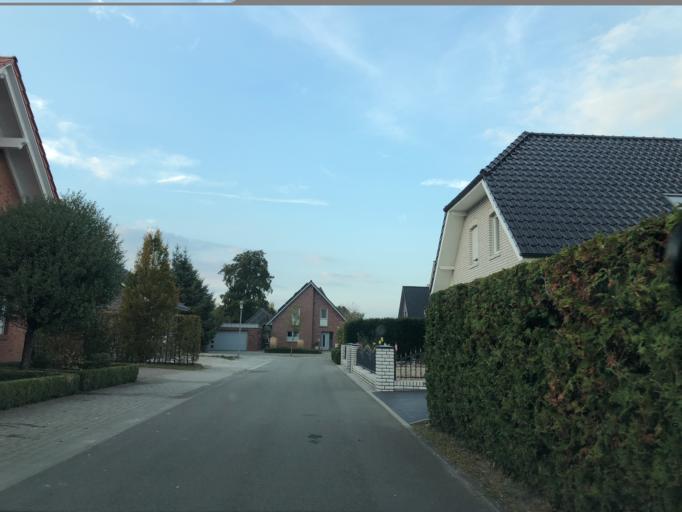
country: DE
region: Lower Saxony
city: Papenburg
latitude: 53.0761
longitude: 7.4512
